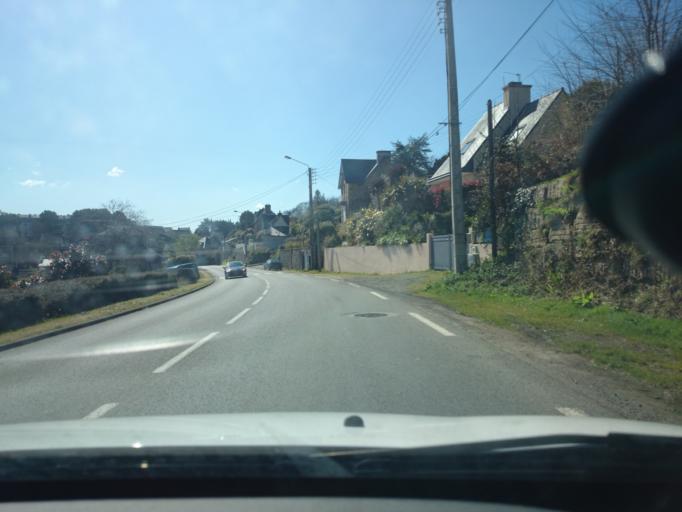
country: FR
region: Brittany
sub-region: Departement des Cotes-d'Armor
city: Perros-Guirec
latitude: 48.8122
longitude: -3.4637
